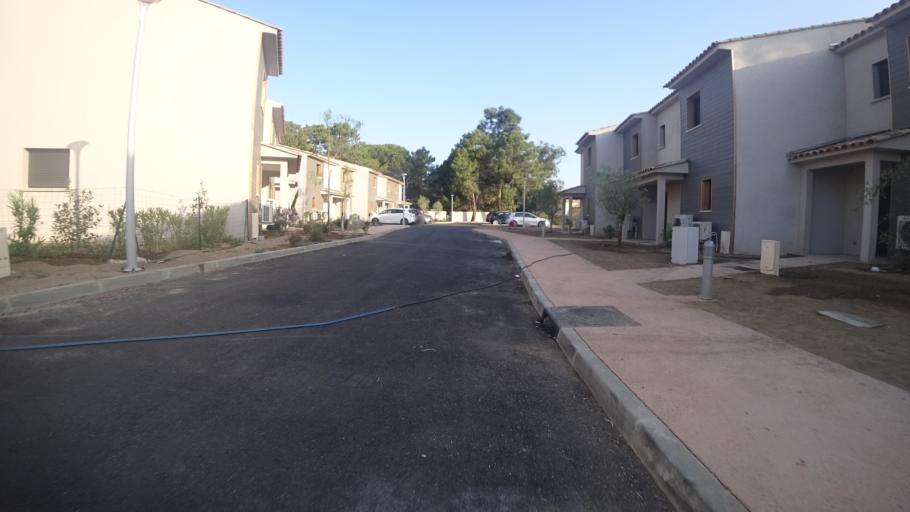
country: FR
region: Corsica
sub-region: Departement de la Corse-du-Sud
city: Porto-Vecchio
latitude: 41.6295
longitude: 9.3353
